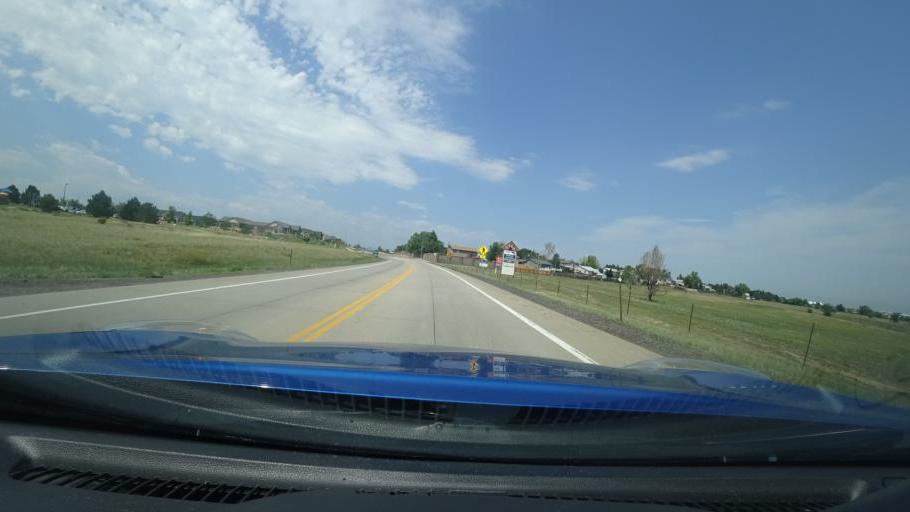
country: US
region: Colorado
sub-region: Adams County
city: Aurora
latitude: 39.6820
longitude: -104.7545
